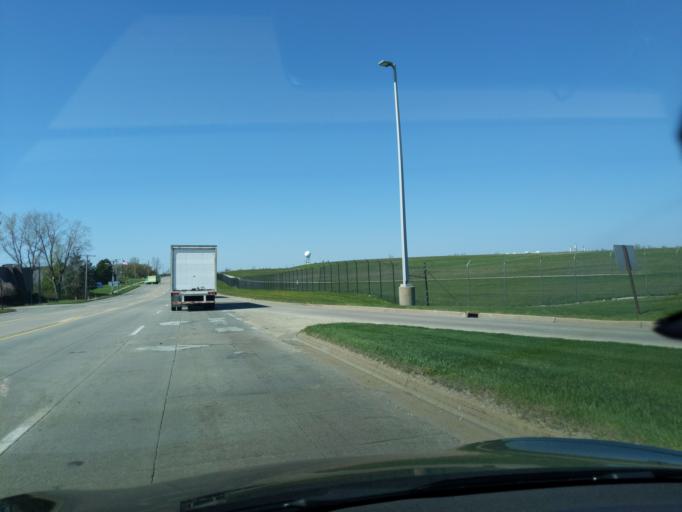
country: US
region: Michigan
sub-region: Kent County
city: East Grand Rapids
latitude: 42.8847
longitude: -85.5471
